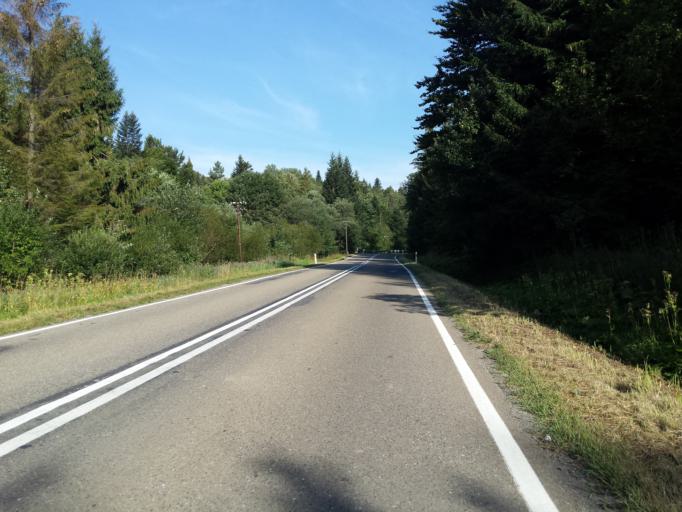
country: PL
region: Subcarpathian Voivodeship
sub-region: Powiat leski
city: Cisna
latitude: 49.2266
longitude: 22.3048
